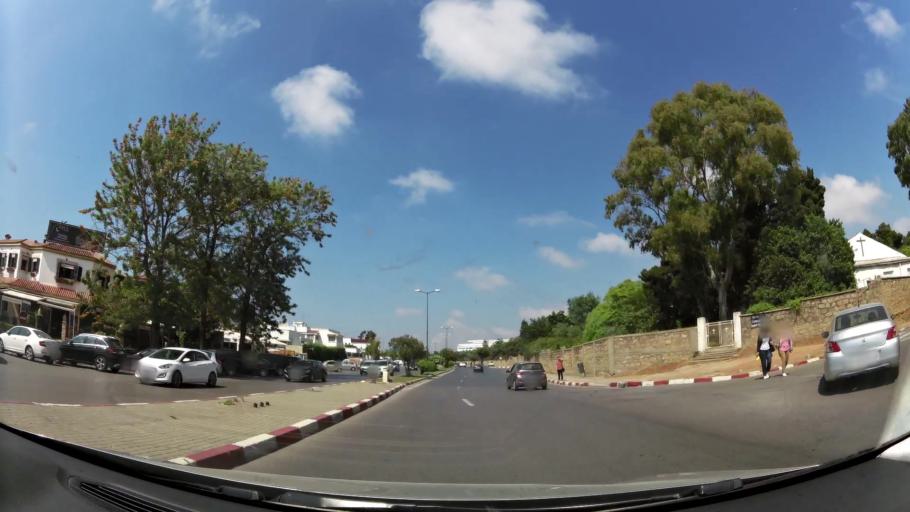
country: MA
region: Rabat-Sale-Zemmour-Zaer
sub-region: Rabat
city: Rabat
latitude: 33.9894
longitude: -6.8480
